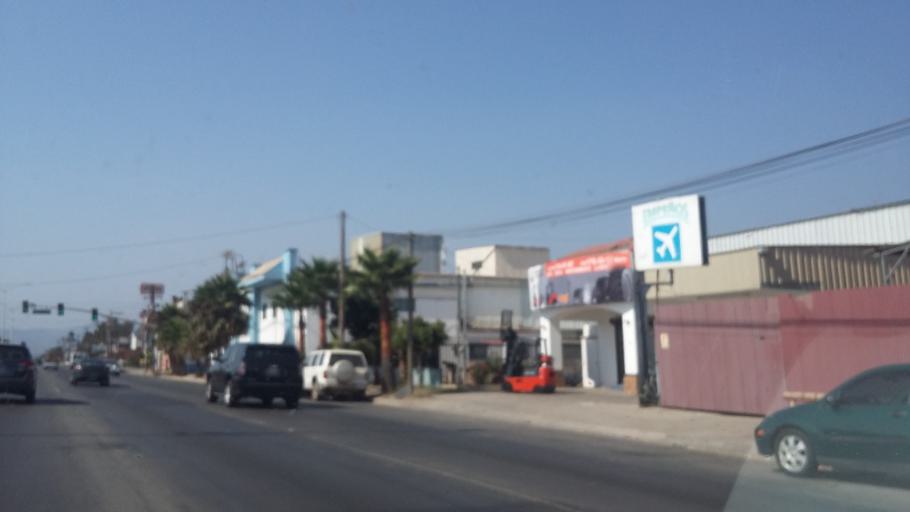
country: MX
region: Baja California
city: Ensenada
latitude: 31.7956
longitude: -116.5937
